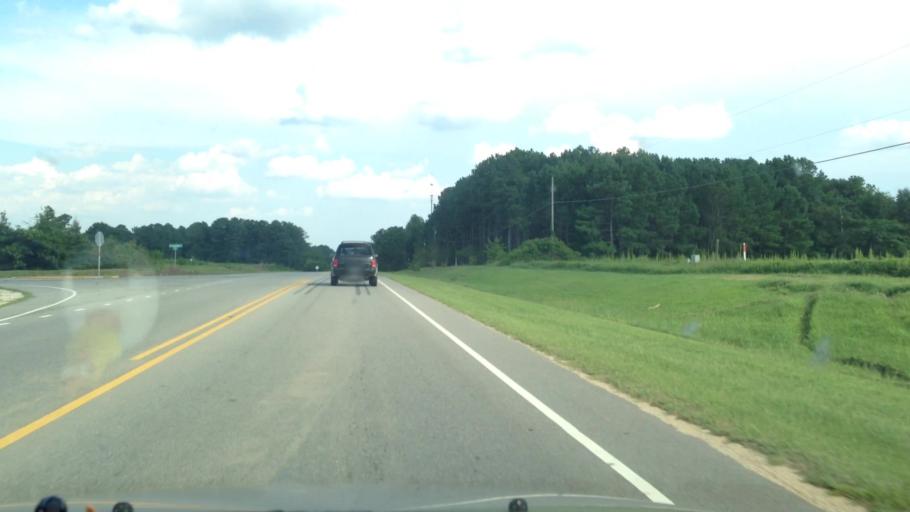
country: US
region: North Carolina
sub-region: Harnett County
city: Lillington
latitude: 35.4142
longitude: -78.8689
